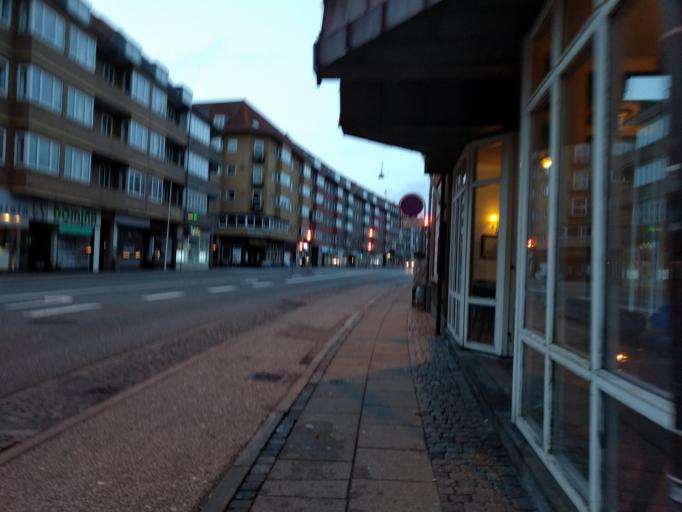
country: DK
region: North Denmark
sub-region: Alborg Kommune
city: Aalborg
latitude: 57.0483
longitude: 9.9157
